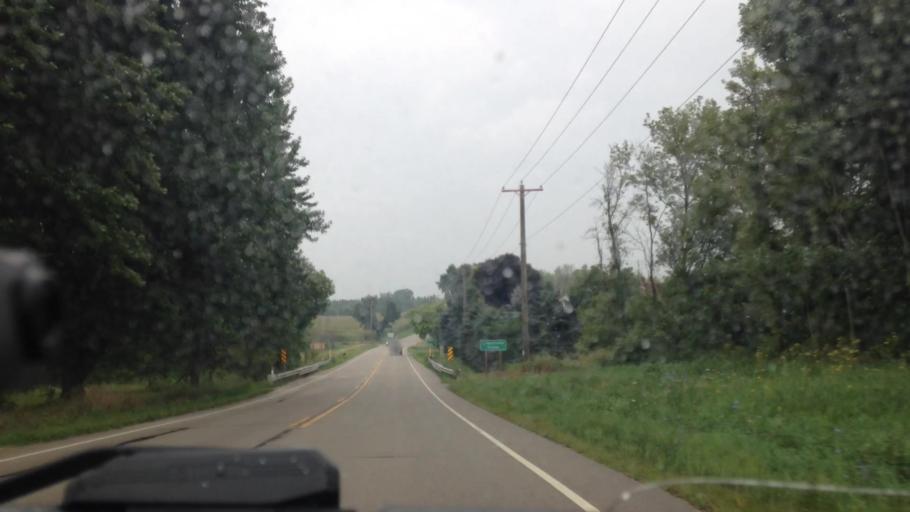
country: US
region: Wisconsin
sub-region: Washington County
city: Hartford
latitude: 43.4015
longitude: -88.3646
